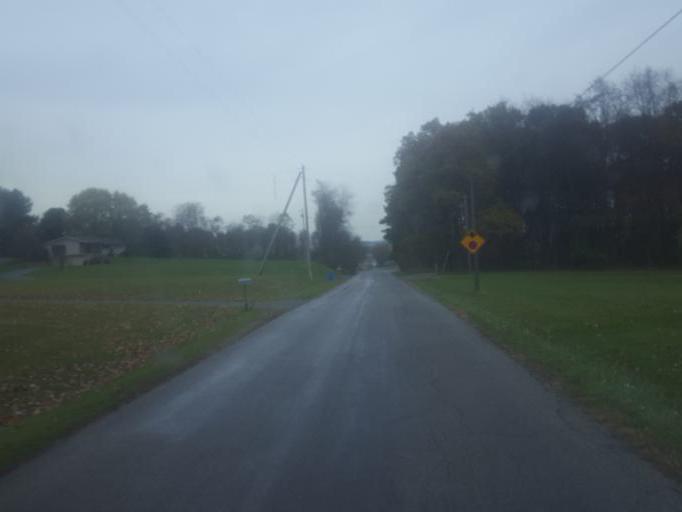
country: US
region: Ohio
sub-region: Wayne County
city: Shreve
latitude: 40.7815
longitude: -82.1175
